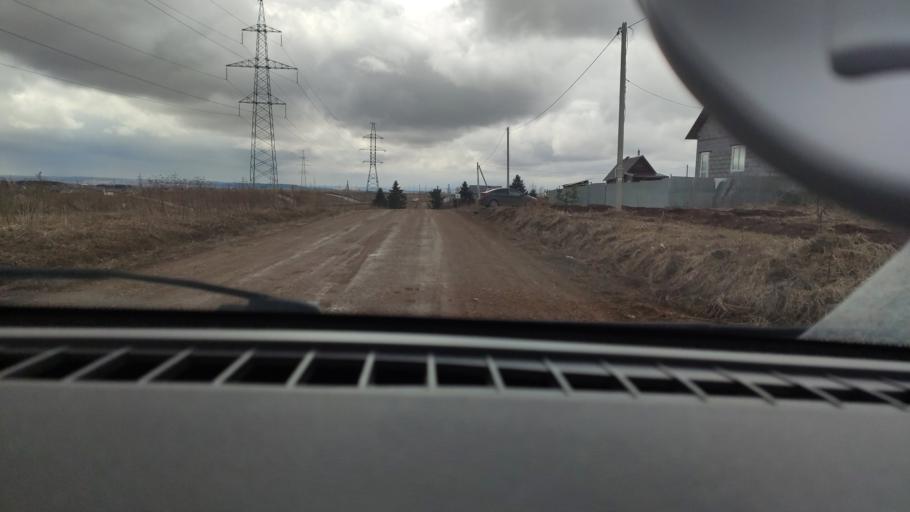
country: RU
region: Perm
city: Ferma
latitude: 57.9435
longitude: 56.3474
